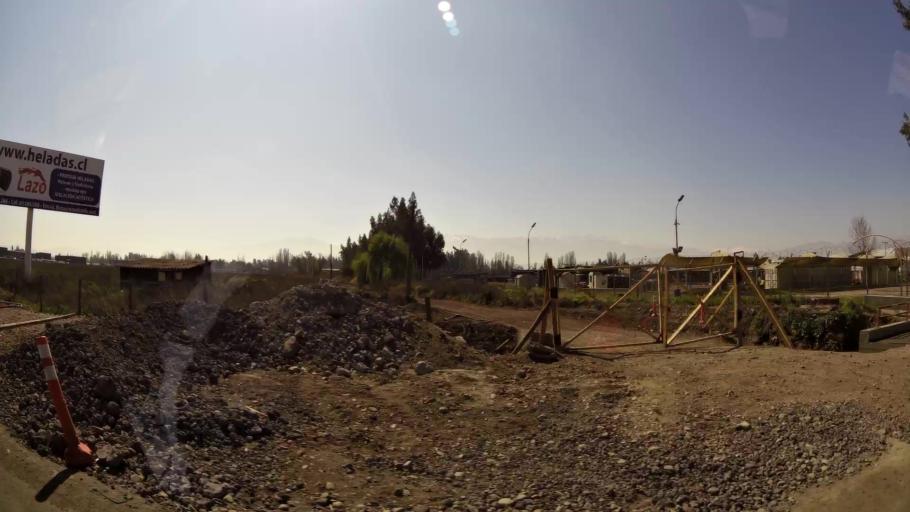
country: CL
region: Santiago Metropolitan
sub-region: Provincia de Chacabuco
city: Chicureo Abajo
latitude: -33.2823
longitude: -70.7374
